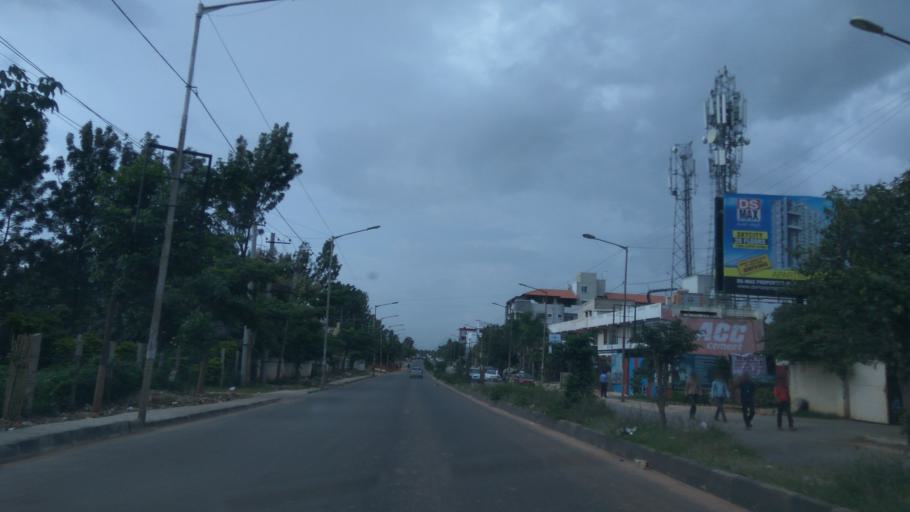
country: IN
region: Karnataka
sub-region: Bangalore Urban
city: Yelahanka
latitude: 13.0806
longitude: 77.6341
